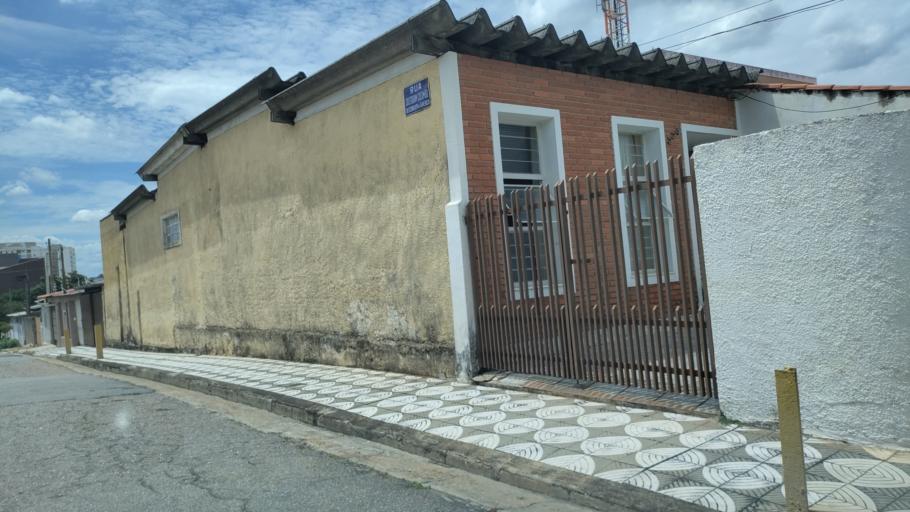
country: BR
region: Sao Paulo
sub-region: Sorocaba
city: Sorocaba
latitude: -23.4801
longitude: -47.4475
